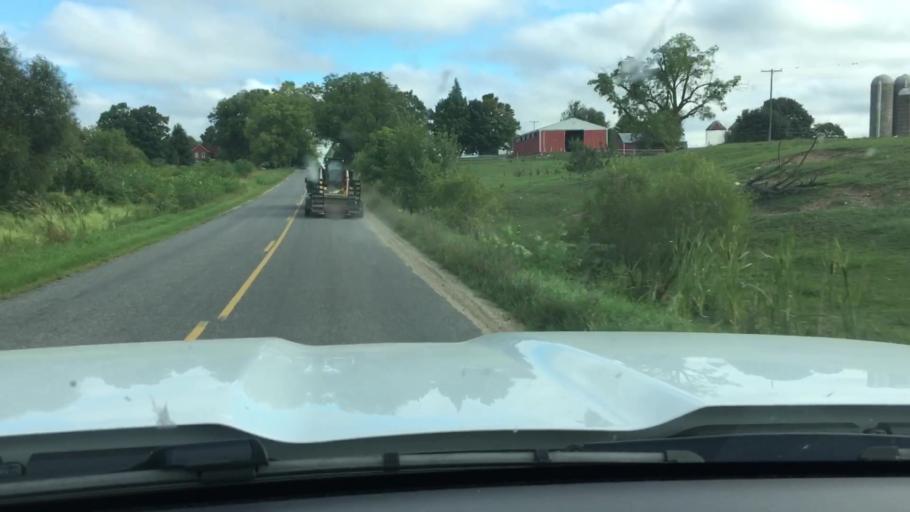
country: US
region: Michigan
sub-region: Kent County
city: Byron Center
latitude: 42.8073
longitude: -85.8026
